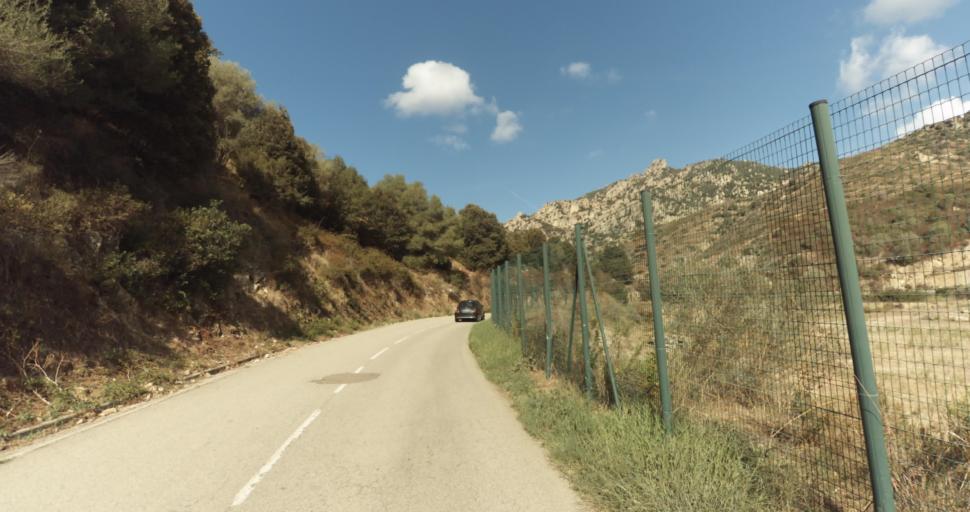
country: FR
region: Corsica
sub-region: Departement de la Corse-du-Sud
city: Ajaccio
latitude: 41.9314
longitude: 8.6924
